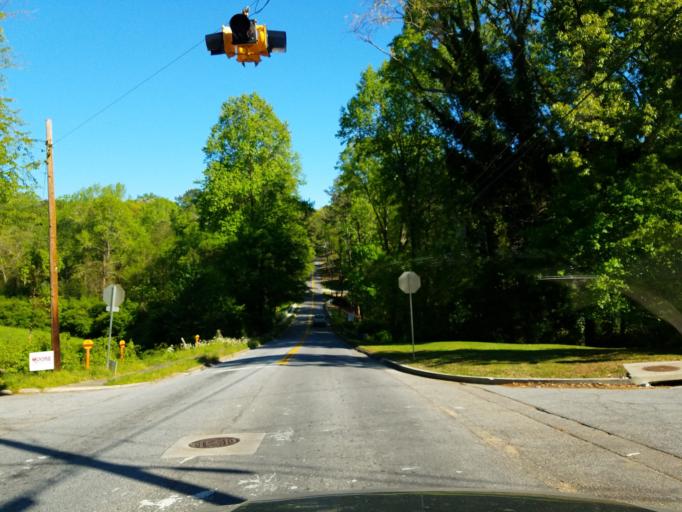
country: US
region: Georgia
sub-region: Cobb County
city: Smyrna
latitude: 33.8562
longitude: -84.5302
